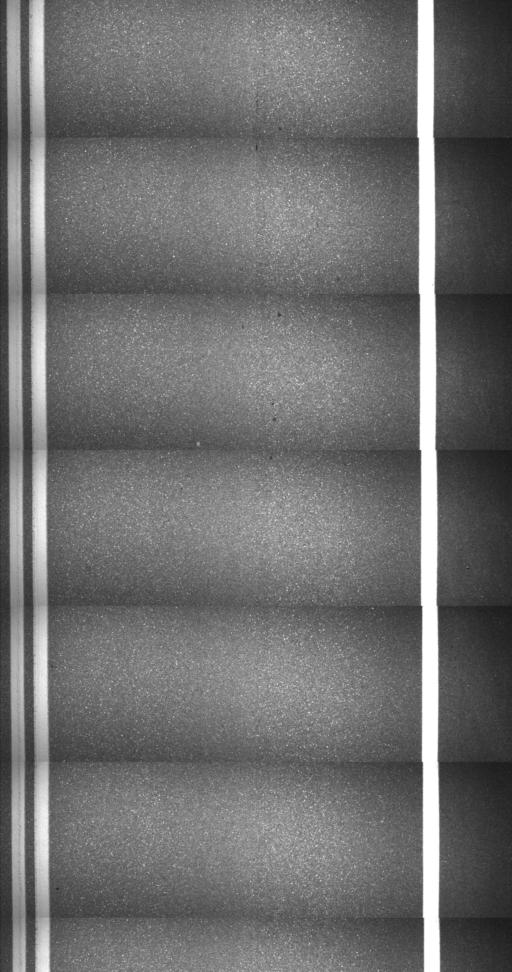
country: US
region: Vermont
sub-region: Windham County
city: Dover
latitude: 43.0137
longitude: -72.8618
